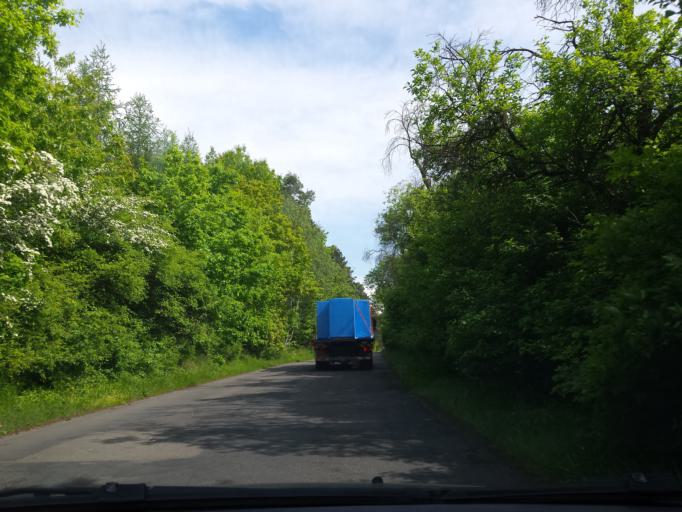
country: CZ
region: Central Bohemia
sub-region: Okres Melnik
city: Melnik
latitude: 50.3787
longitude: 14.4930
